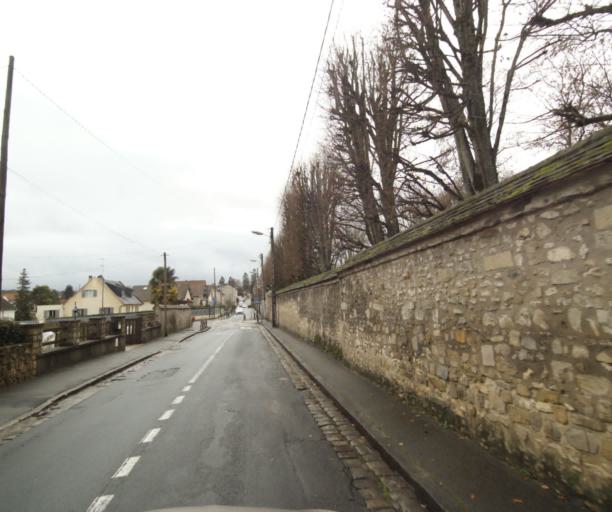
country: FR
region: Ile-de-France
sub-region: Departement de Seine-et-Marne
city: Avon
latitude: 48.4089
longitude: 2.7197
